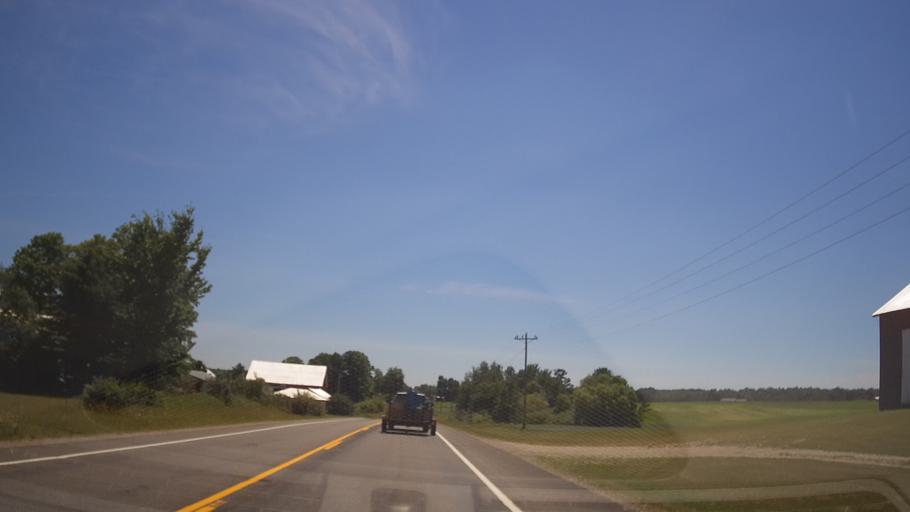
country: US
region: Michigan
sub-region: Grand Traverse County
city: Kingsley
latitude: 44.6069
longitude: -85.6965
